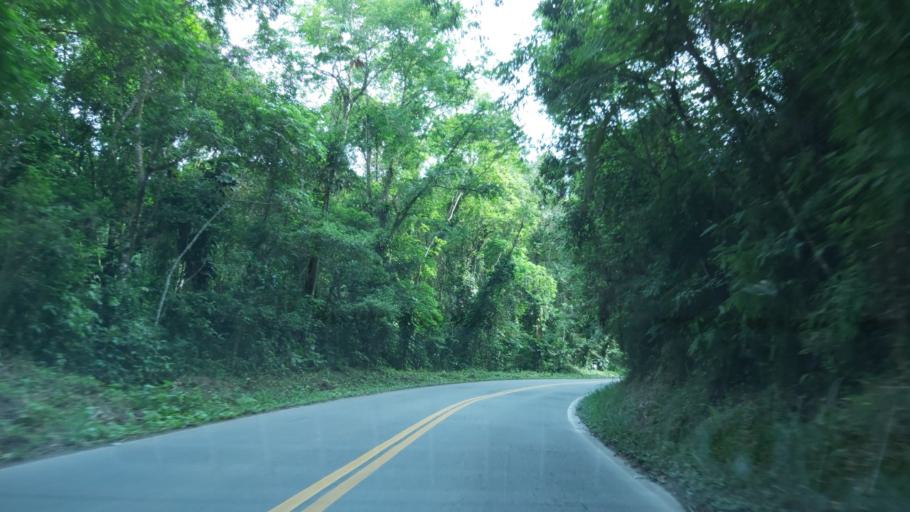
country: BR
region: Sao Paulo
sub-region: Juquia
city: Juquia
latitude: -24.1025
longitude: -47.6270
